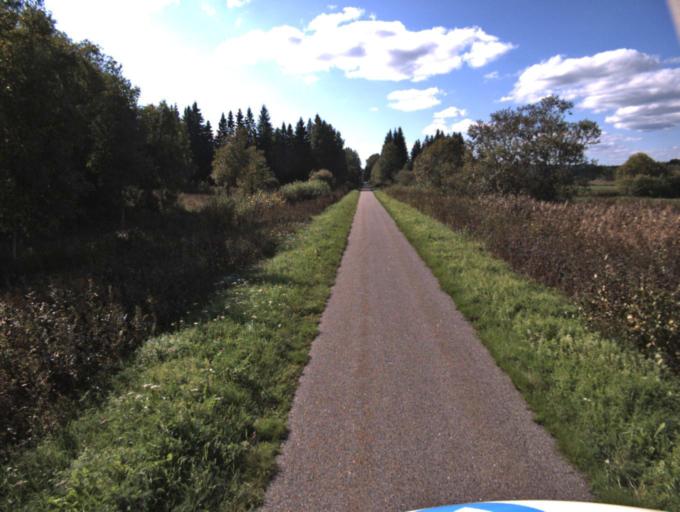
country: SE
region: Vaestra Goetaland
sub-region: Ulricehamns Kommun
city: Ulricehamn
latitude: 57.8361
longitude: 13.2530
